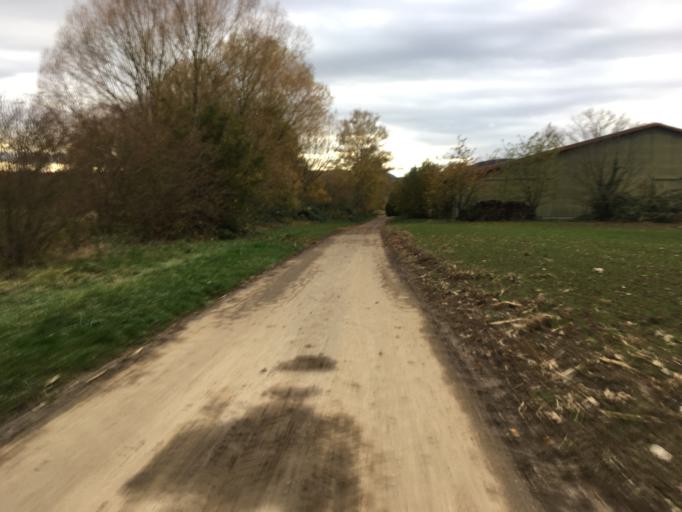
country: DE
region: Baden-Wuerttemberg
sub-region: Freiburg Region
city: Botzingen
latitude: 48.0712
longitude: 7.7319
